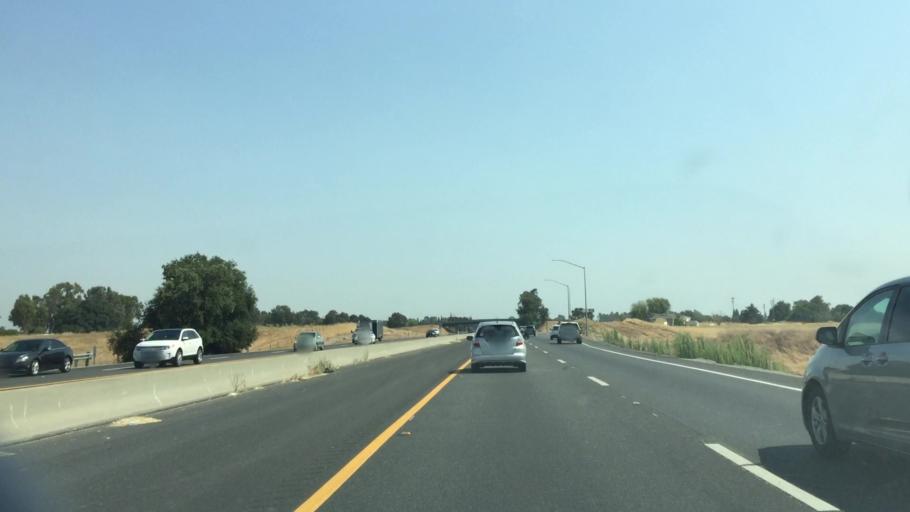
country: US
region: California
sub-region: Sacramento County
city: Galt
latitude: 38.2373
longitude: -121.2829
